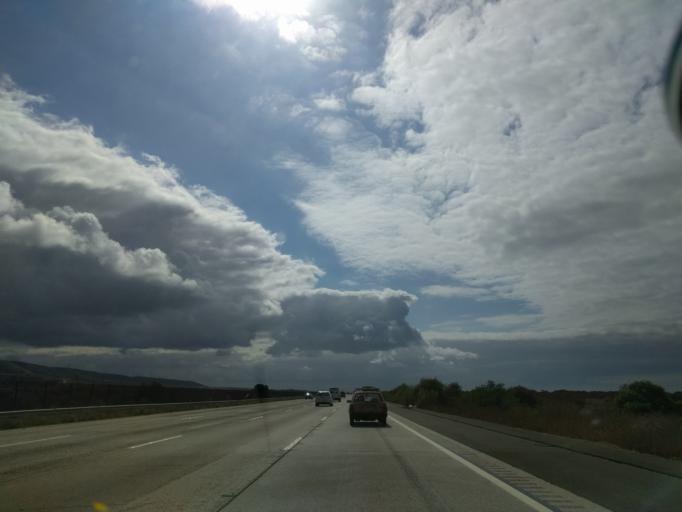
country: US
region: California
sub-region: Orange County
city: San Clemente
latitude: 33.3359
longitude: -117.5026
